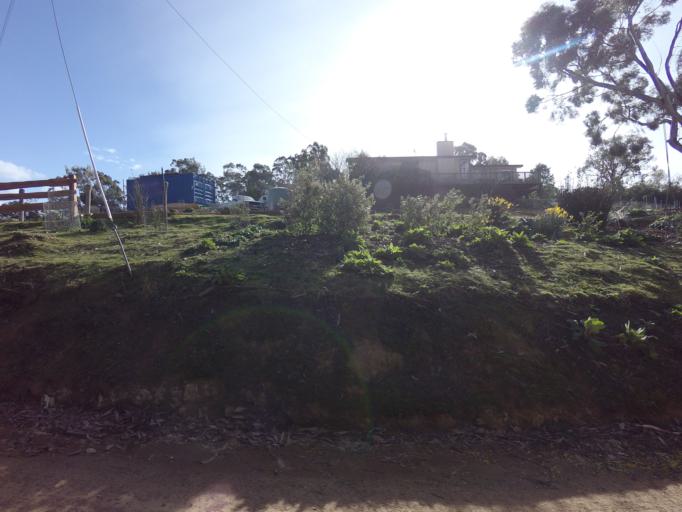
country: AU
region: Tasmania
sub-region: Kingborough
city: Kettering
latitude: -43.1209
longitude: 147.2627
